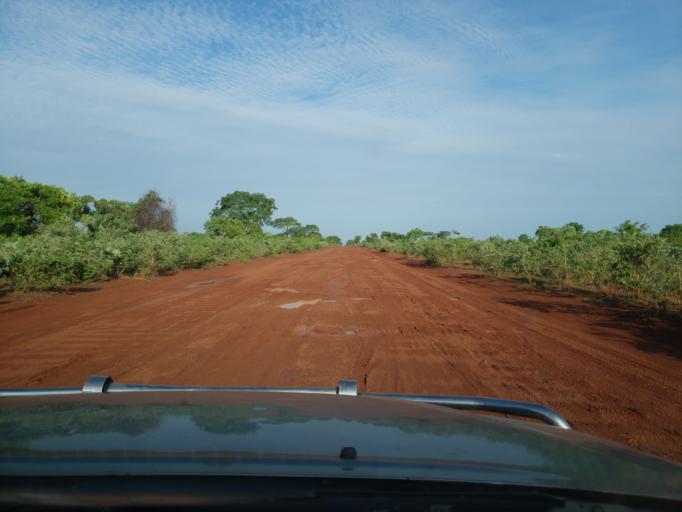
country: ML
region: Sikasso
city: Koutiala
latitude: 12.4281
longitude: -5.6269
